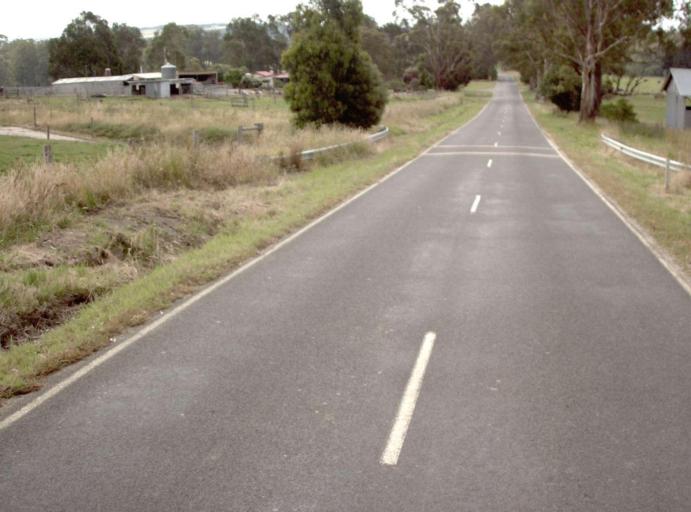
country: AU
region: Victoria
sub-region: Latrobe
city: Traralgon
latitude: -38.3819
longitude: 146.7946
